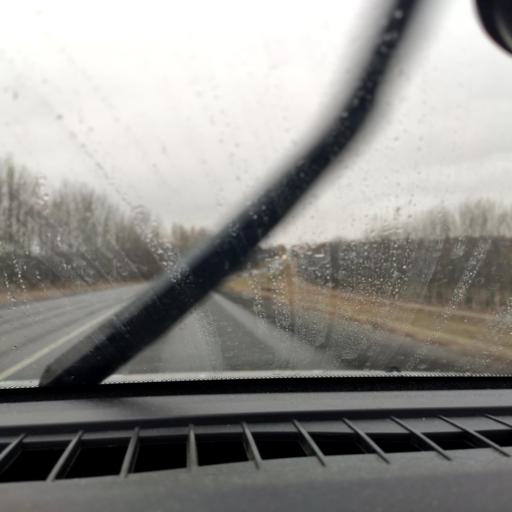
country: RU
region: Belgorod
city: Alekseyevka
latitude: 50.6481
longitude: 38.6739
